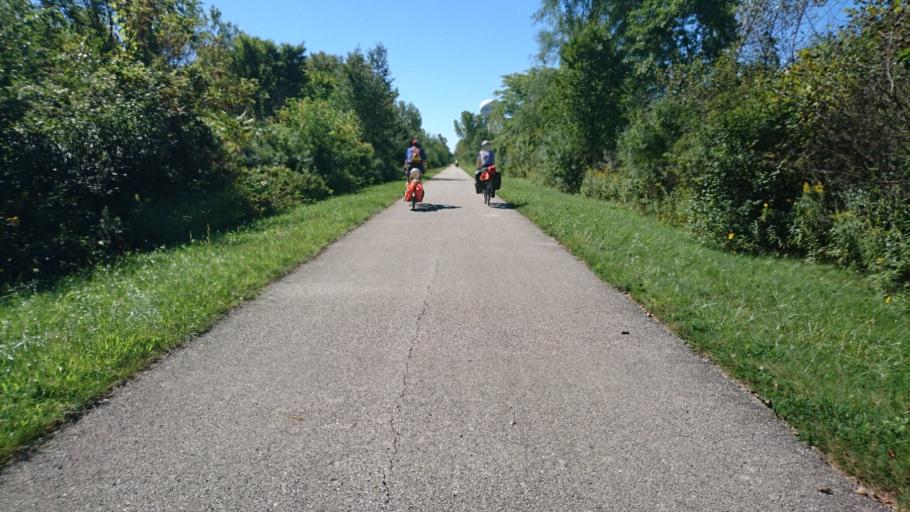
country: US
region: Illinois
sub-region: Cook County
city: Lansing
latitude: 41.5911
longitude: -87.5494
